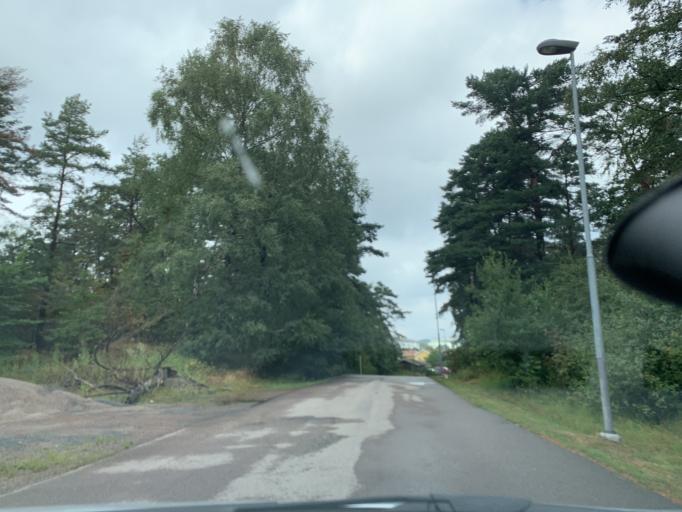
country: SE
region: Vaestra Goetaland
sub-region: Goteborg
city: Eriksbo
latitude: 57.7417
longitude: 12.0340
